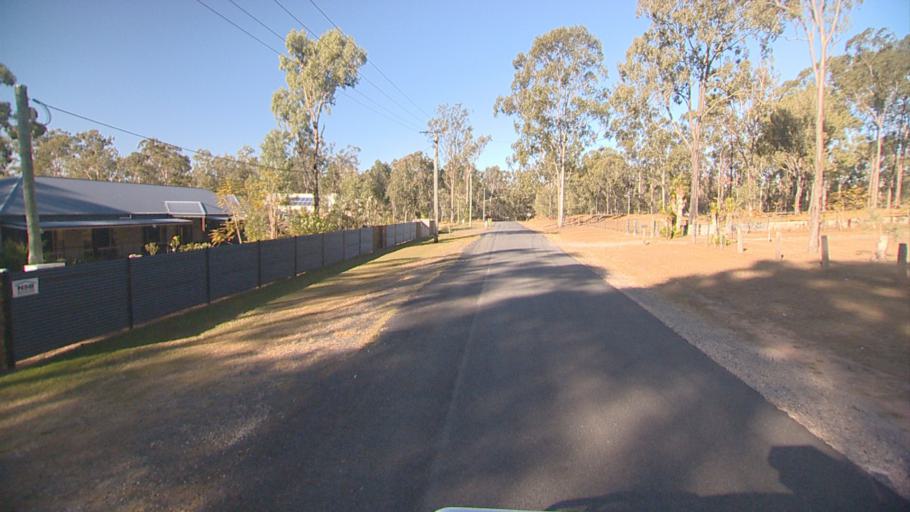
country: AU
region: Queensland
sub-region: Logan
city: North Maclean
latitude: -27.7960
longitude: 153.0244
